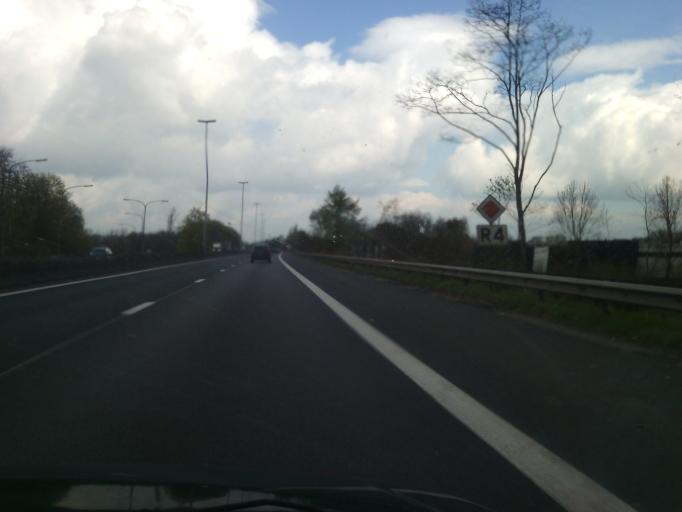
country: BE
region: Flanders
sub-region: Provincie Oost-Vlaanderen
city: Destelbergen
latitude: 51.0660
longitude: 3.8099
